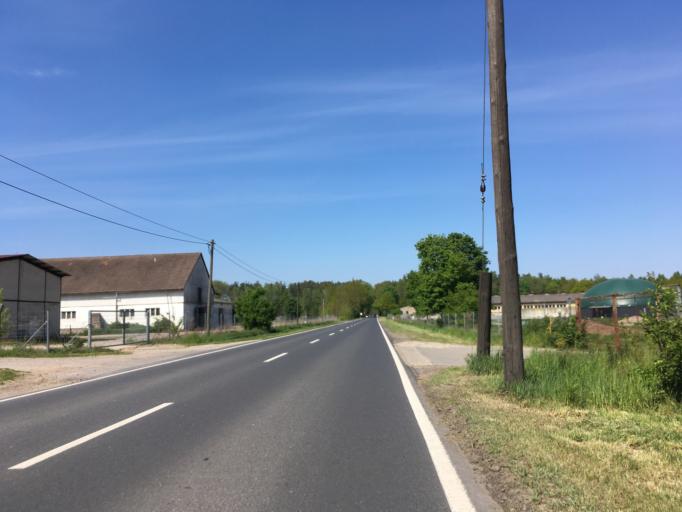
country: DE
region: Brandenburg
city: Rudnitz
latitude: 52.7635
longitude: 13.5656
